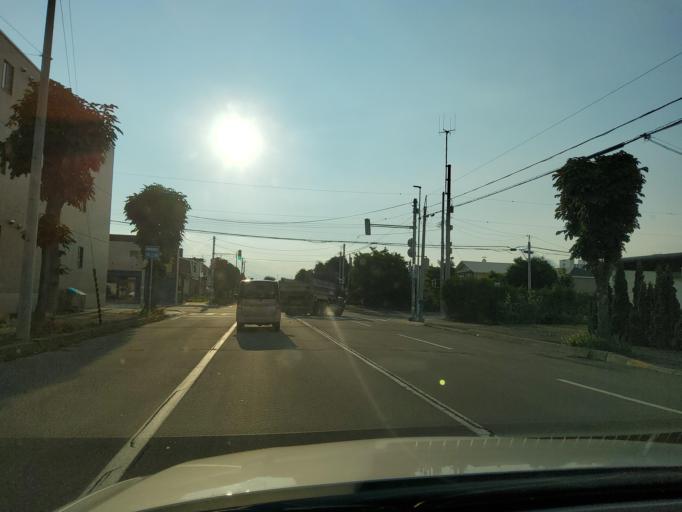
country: JP
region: Hokkaido
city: Obihiro
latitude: 42.9168
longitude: 143.1872
